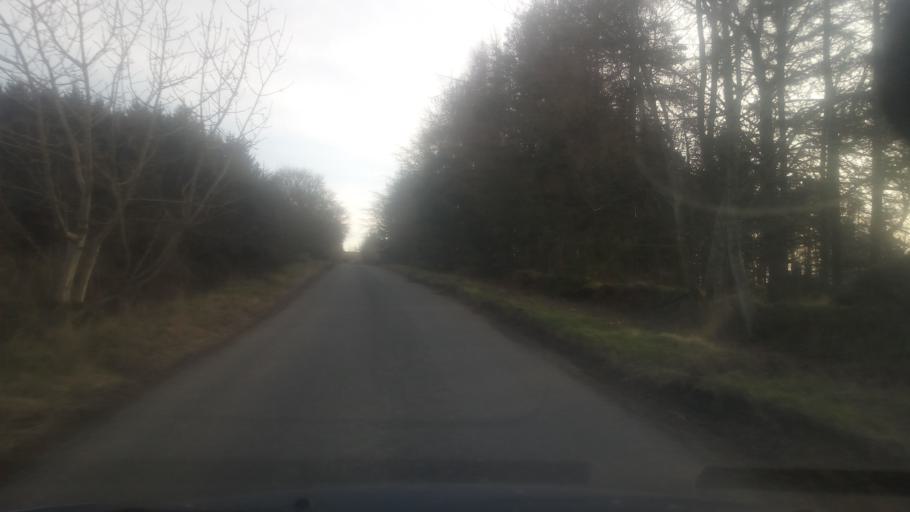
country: GB
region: Scotland
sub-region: The Scottish Borders
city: Jedburgh
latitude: 55.4064
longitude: -2.6005
